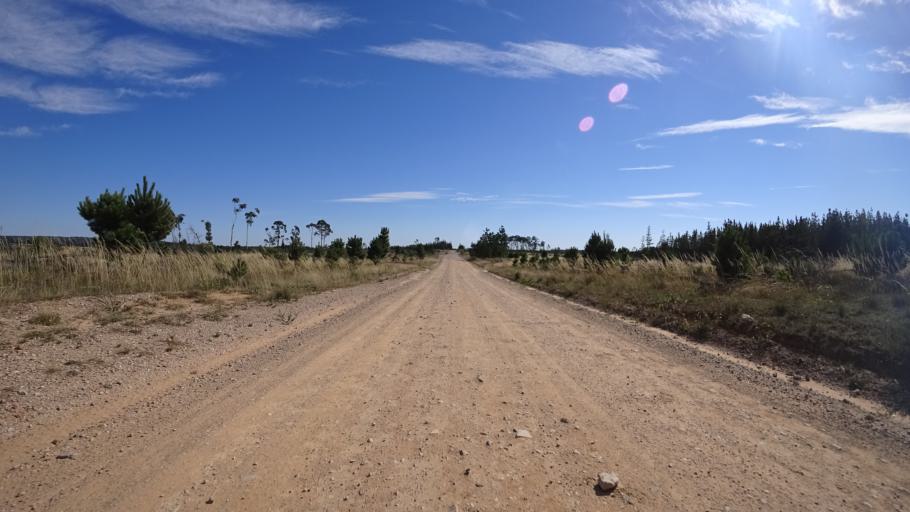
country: AU
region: New South Wales
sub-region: Lithgow
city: Lithgow
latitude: -33.3728
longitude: 150.2453
